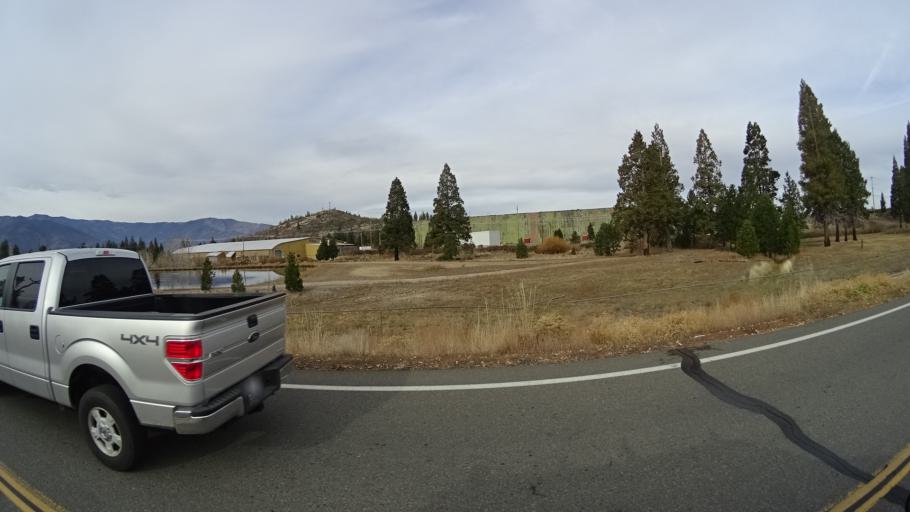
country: US
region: California
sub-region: Siskiyou County
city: Weed
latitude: 41.4307
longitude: -122.3830
